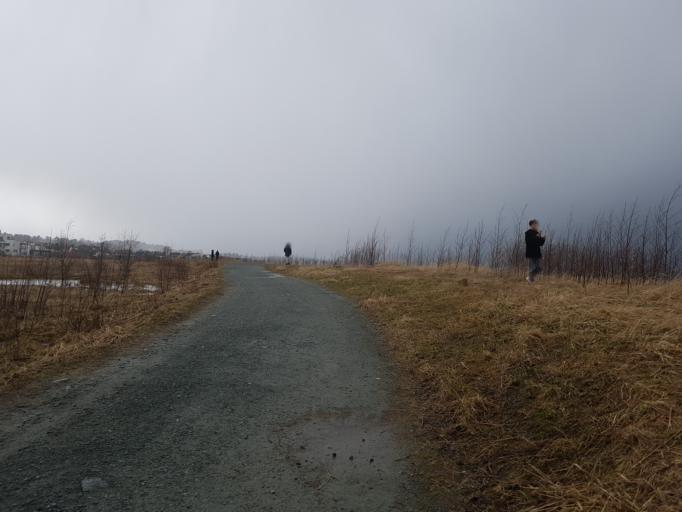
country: NO
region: Sor-Trondelag
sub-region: Trondheim
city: Trondheim
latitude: 63.4304
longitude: 10.5330
